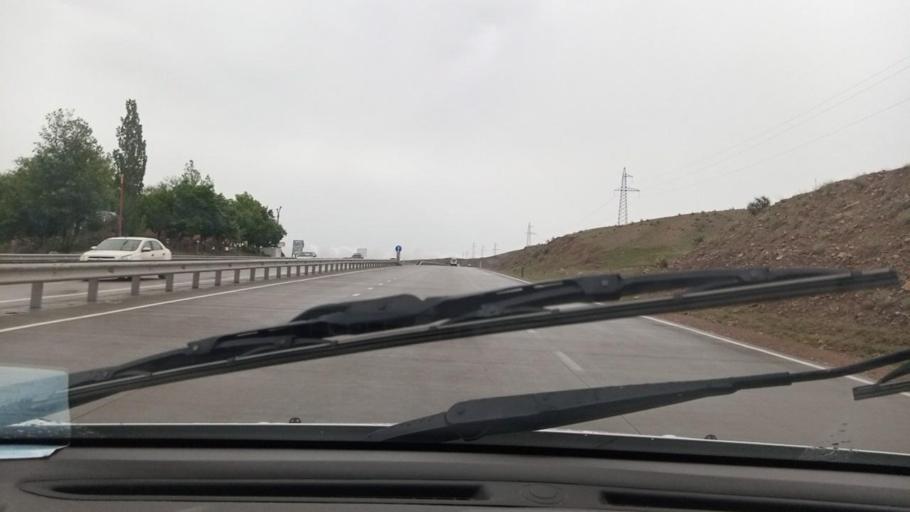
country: UZ
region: Namangan
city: Pop Shahri
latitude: 40.9416
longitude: 70.6891
